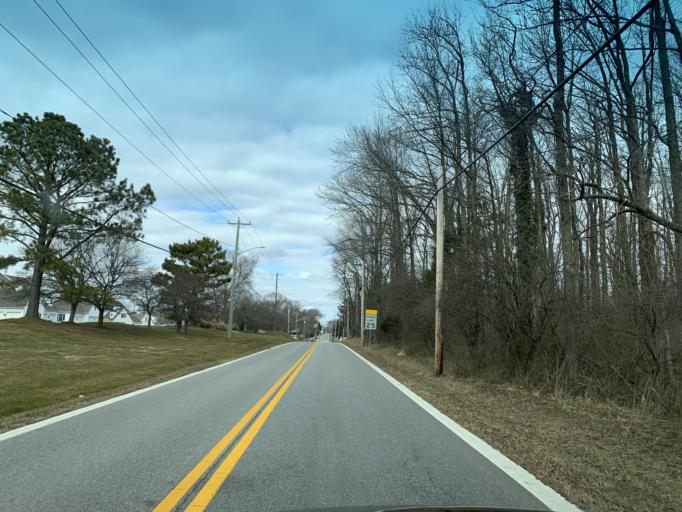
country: US
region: Maryland
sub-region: Queen Anne's County
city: Grasonville
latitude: 38.9861
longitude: -76.1613
